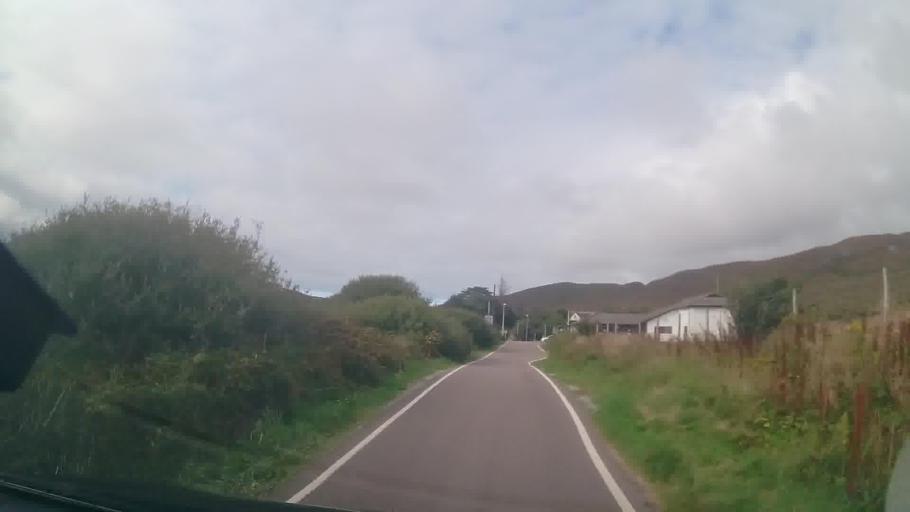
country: GB
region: Scotland
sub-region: Argyll and Bute
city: Isle Of Mull
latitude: 56.6957
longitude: -6.1000
